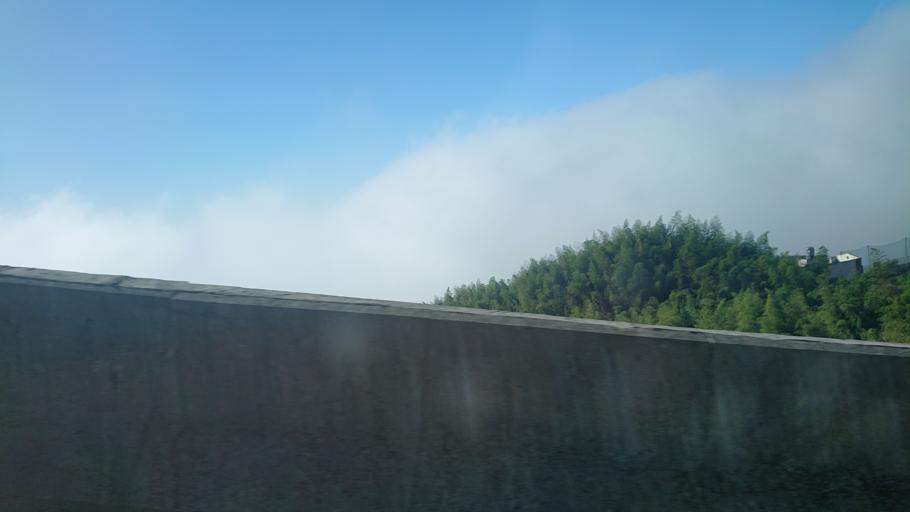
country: TW
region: Taiwan
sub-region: Chiayi
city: Jiayi Shi
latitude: 23.4777
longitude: 120.6985
